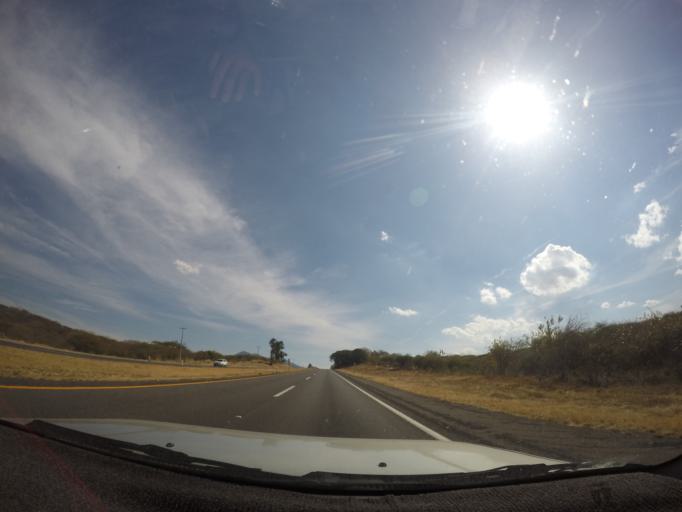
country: MX
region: Michoacan
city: Churintzio
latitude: 20.1157
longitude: -102.0474
